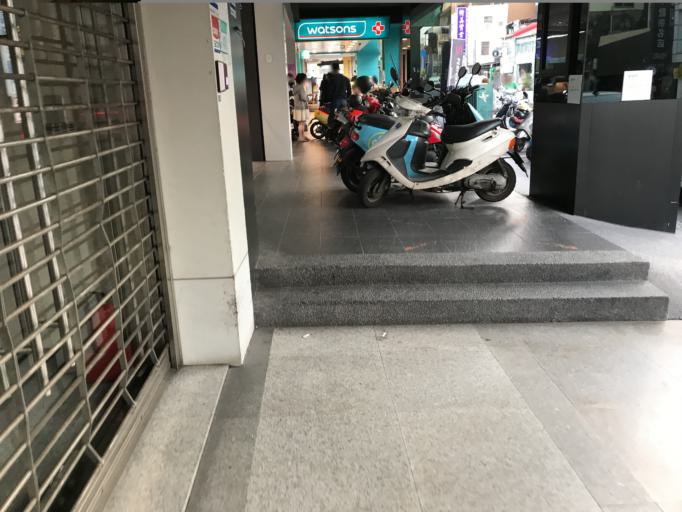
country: TW
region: Taiwan
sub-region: Tainan
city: Tainan
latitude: 22.9950
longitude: 120.2055
